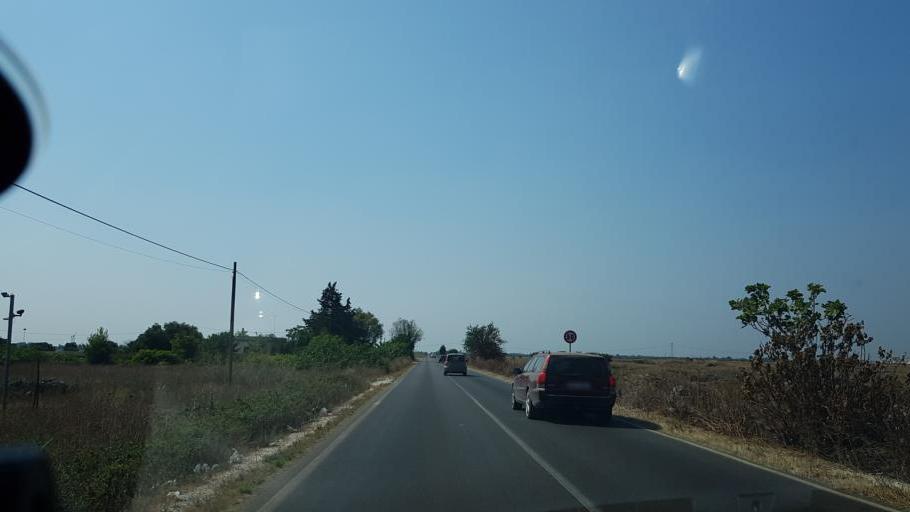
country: IT
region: Apulia
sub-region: Provincia di Taranto
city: Manduria
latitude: 40.4440
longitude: 17.6362
